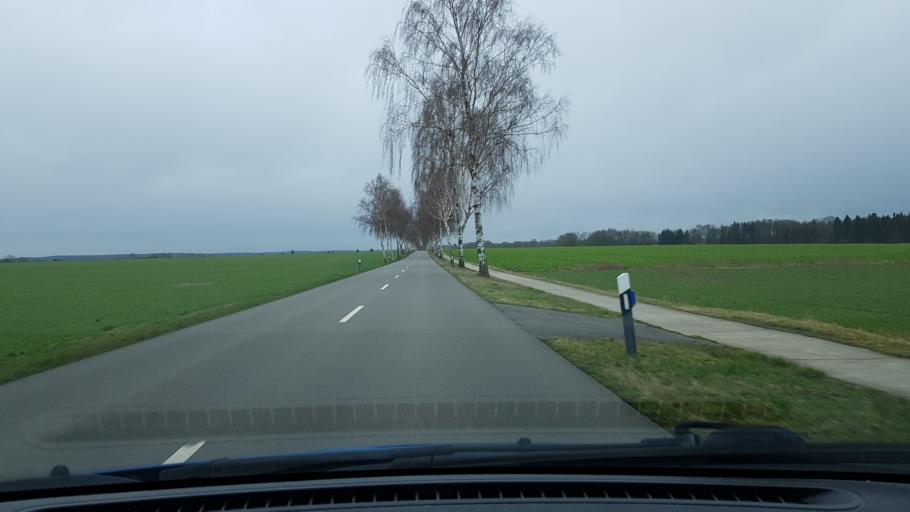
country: DE
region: Lower Saxony
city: Wrestedt
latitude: 52.9190
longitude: 10.5692
